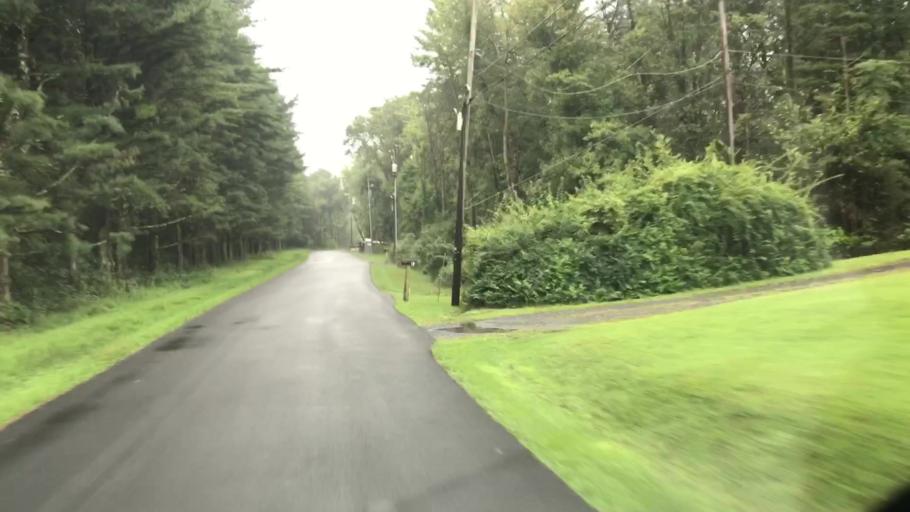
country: US
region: Pennsylvania
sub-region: Perry County
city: Newport
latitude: 40.4066
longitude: -77.1039
